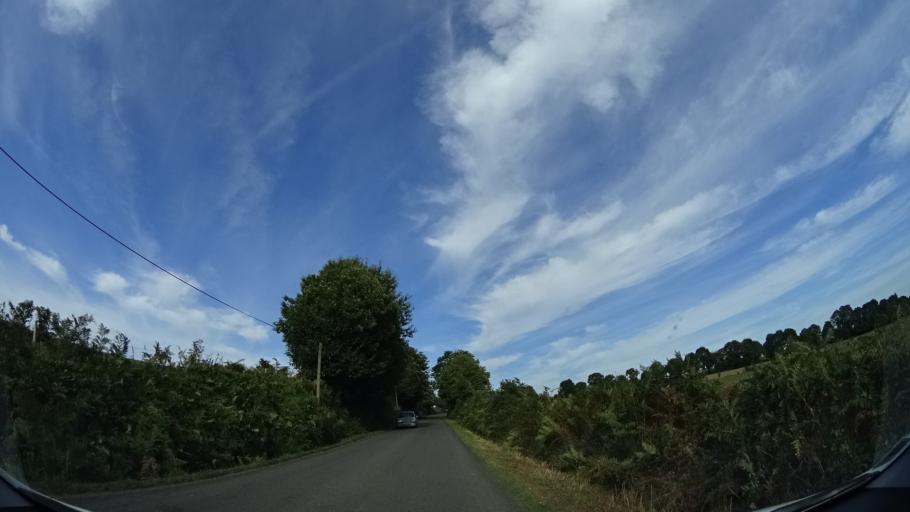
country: FR
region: Brittany
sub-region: Departement d'Ille-et-Vilaine
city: Javene
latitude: 48.3386
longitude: -1.2310
